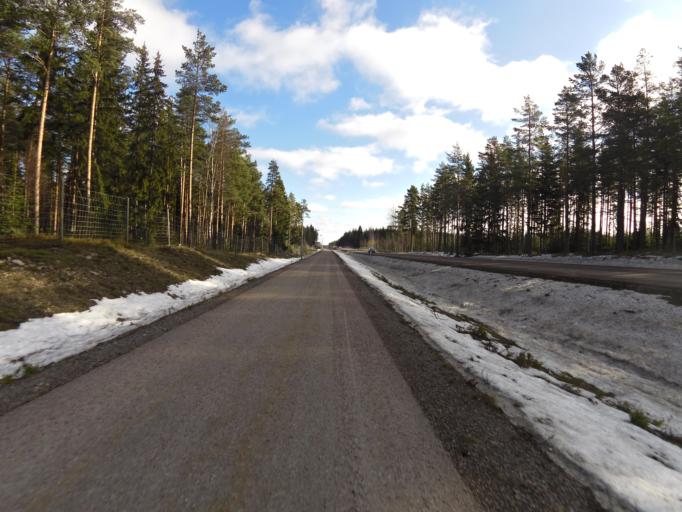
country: SE
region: Uppsala
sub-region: Alvkarleby Kommun
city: Skutskaer
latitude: 60.6466
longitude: 17.2810
